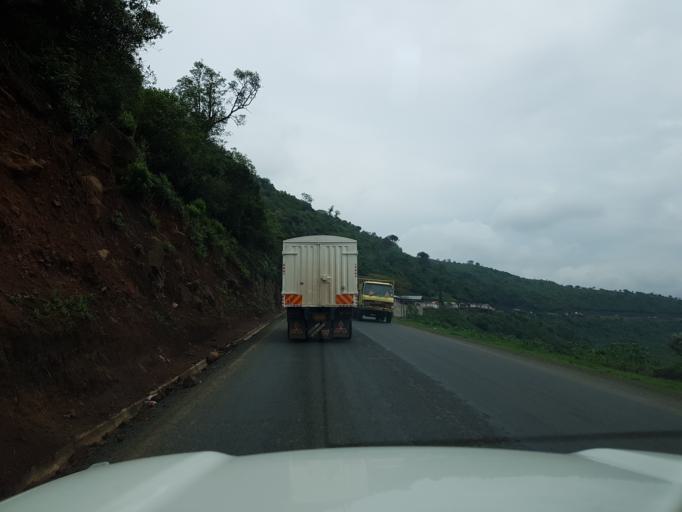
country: KE
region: Kiambu
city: Limuru
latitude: -1.0546
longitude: 36.6021
